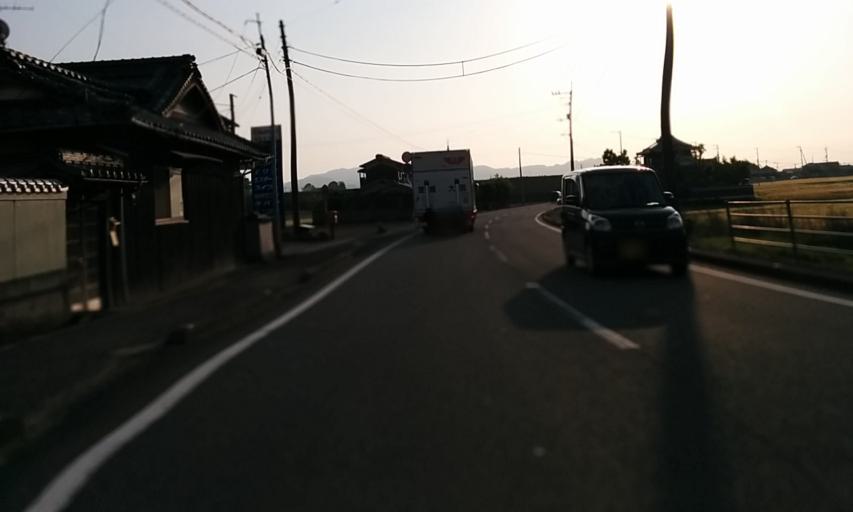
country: JP
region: Ehime
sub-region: Shikoku-chuo Shi
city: Matsuyama
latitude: 33.7742
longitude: 132.8438
